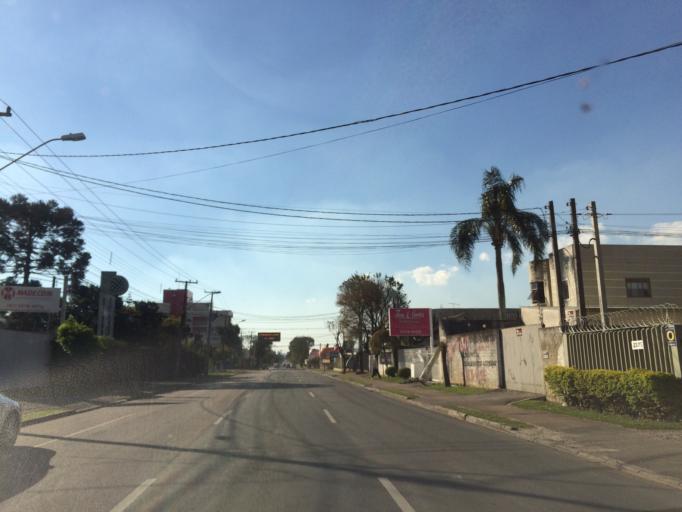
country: BR
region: Parana
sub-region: Sao Jose Dos Pinhais
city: Sao Jose dos Pinhais
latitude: -25.4944
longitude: -49.2397
